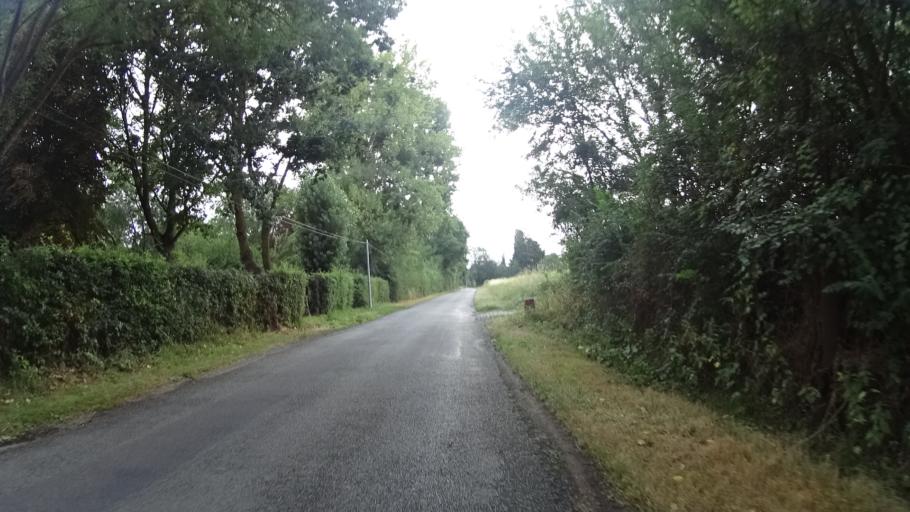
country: FR
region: Pays de la Loire
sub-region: Departement de la Loire-Atlantique
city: Ancenis
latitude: 47.3649
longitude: -1.1589
